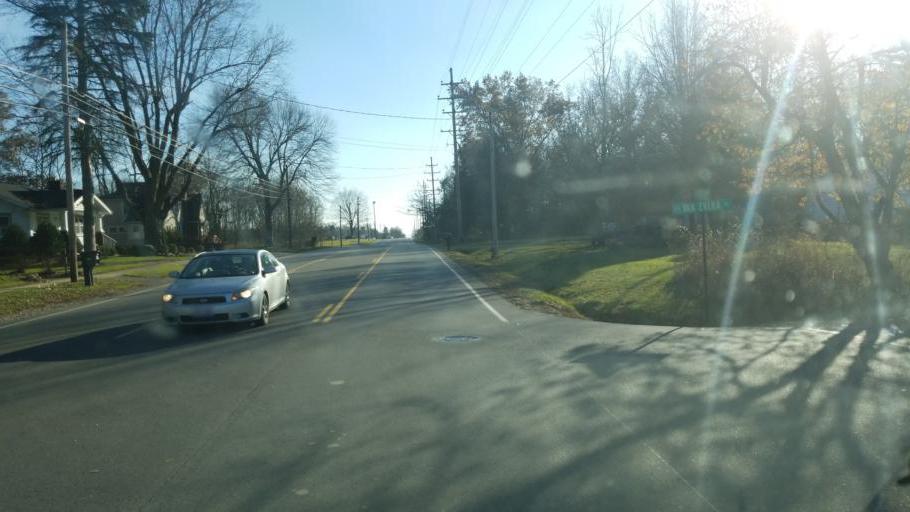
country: US
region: Ohio
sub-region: Summit County
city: Tallmadge
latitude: 41.0901
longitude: -81.4414
